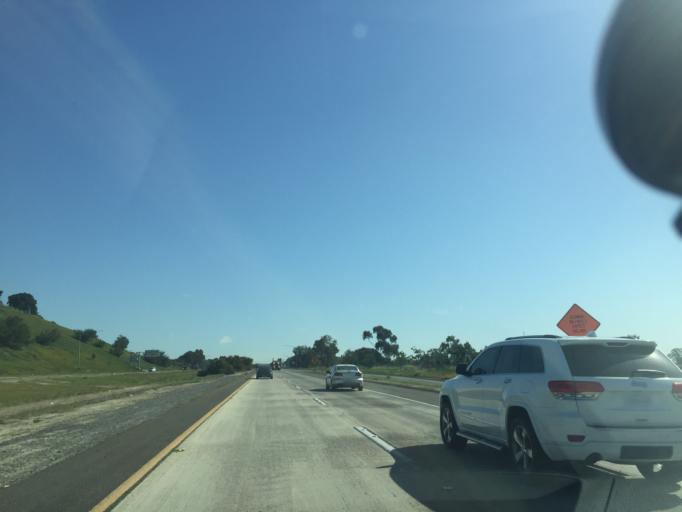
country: US
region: California
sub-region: San Diego County
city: Imperial Beach
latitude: 32.5681
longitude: -117.0517
